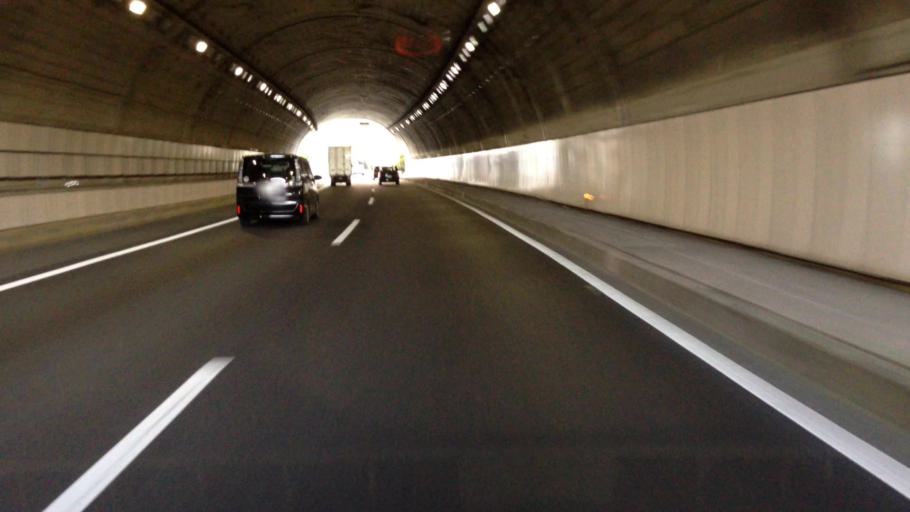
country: JP
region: Kanagawa
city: Zushi
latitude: 35.3228
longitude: 139.6024
